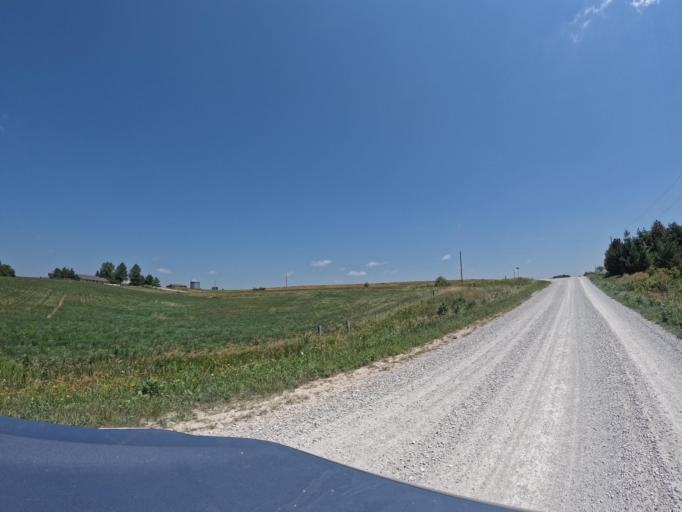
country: US
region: Iowa
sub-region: Keokuk County
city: Sigourney
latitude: 41.2579
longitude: -92.1705
